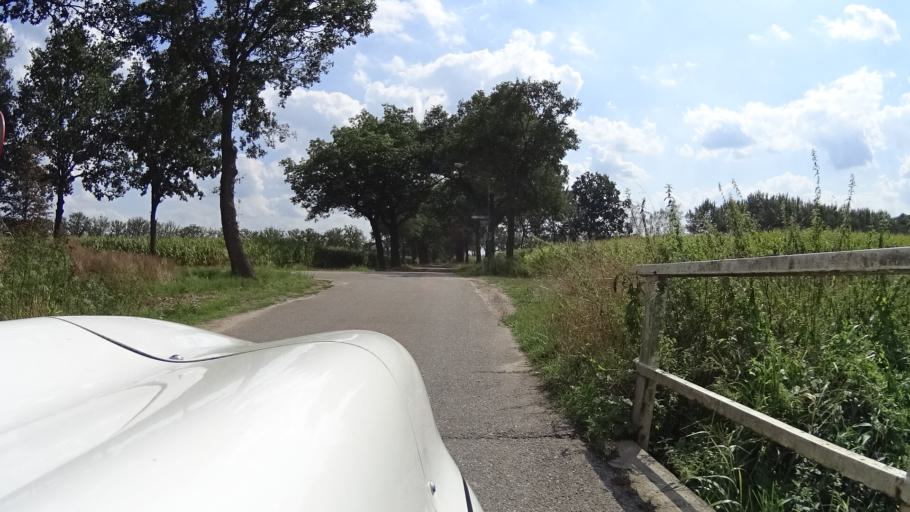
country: NL
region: North Brabant
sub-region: Gemeente Veghel
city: Mariaheide
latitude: 51.6479
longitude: 5.5567
